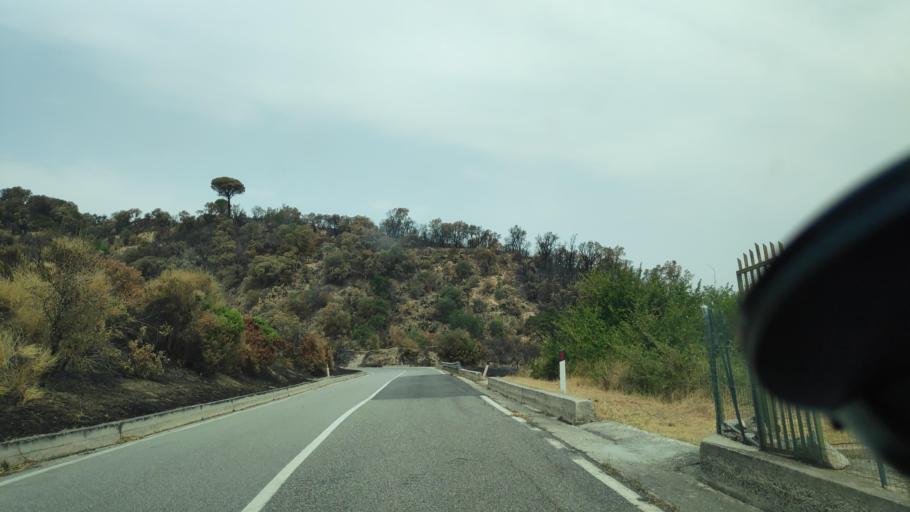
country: IT
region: Calabria
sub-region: Provincia di Catanzaro
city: Sant'Andrea Apostolo dello Ionio
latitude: 38.6413
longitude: 16.5221
